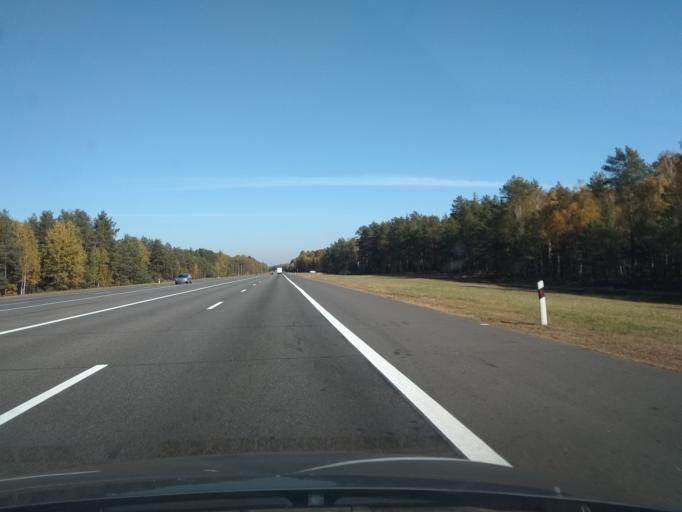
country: BY
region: Brest
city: Ivatsevichy
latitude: 52.7599
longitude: 25.5181
